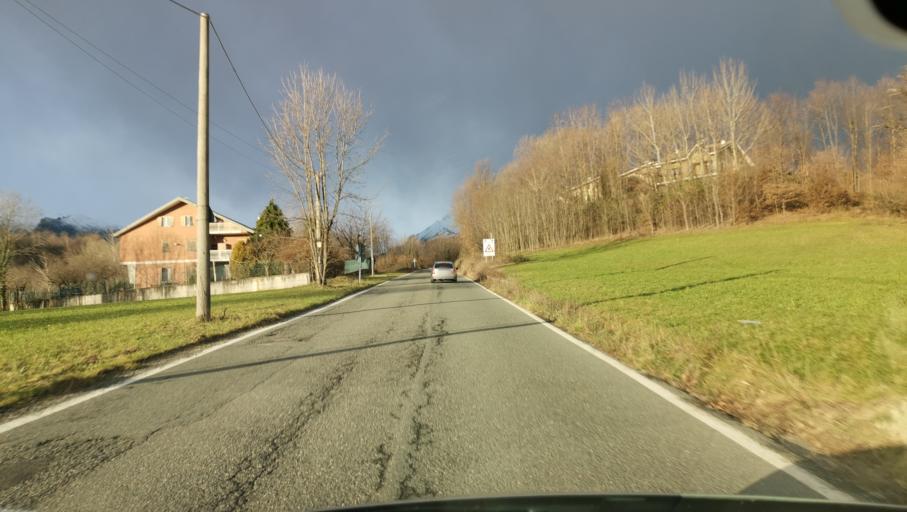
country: IT
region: Piedmont
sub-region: Provincia di Torino
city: Giaveno
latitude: 45.0500
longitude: 7.3329
